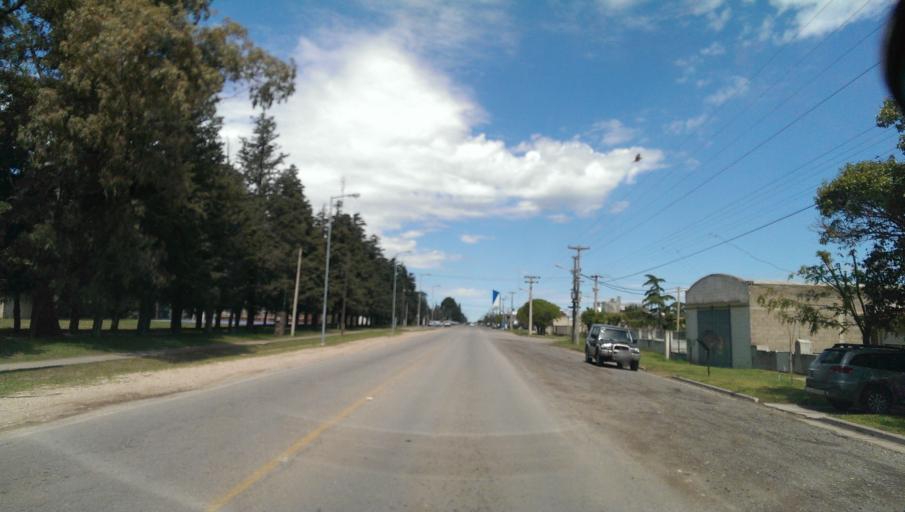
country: AR
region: Buenos Aires
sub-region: Partido de Tornquist
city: Tornquist
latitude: -38.0976
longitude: -62.2182
